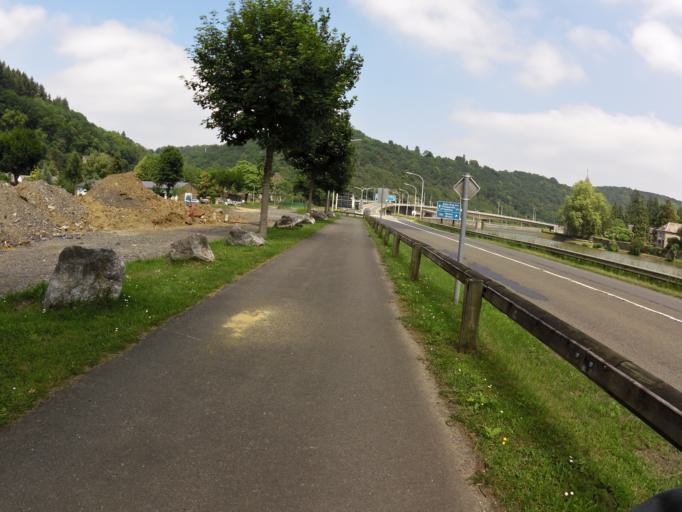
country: BE
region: Wallonia
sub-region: Province de Namur
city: Hastiere-Lavaux
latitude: 50.2135
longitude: 4.8235
